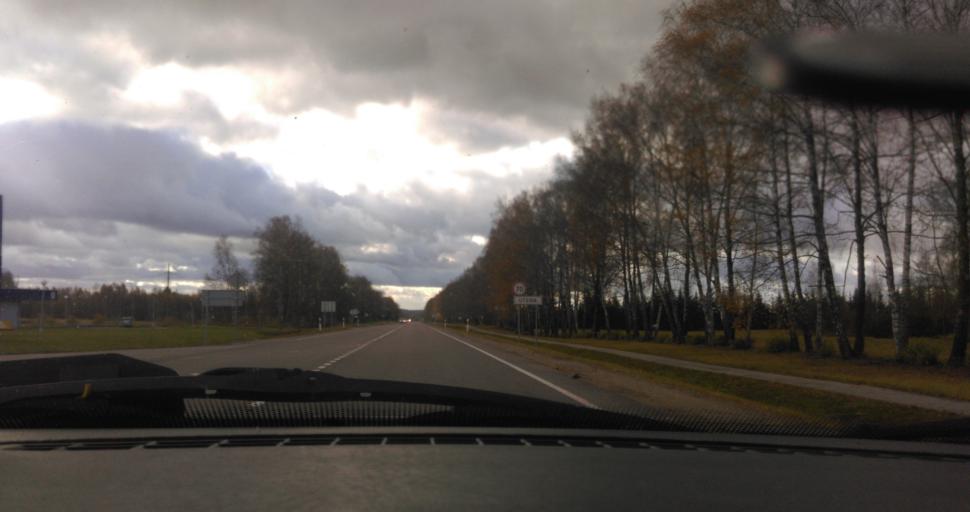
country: LT
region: Utenos apskritis
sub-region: Utena
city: Utena
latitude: 55.5132
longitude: 25.6448
